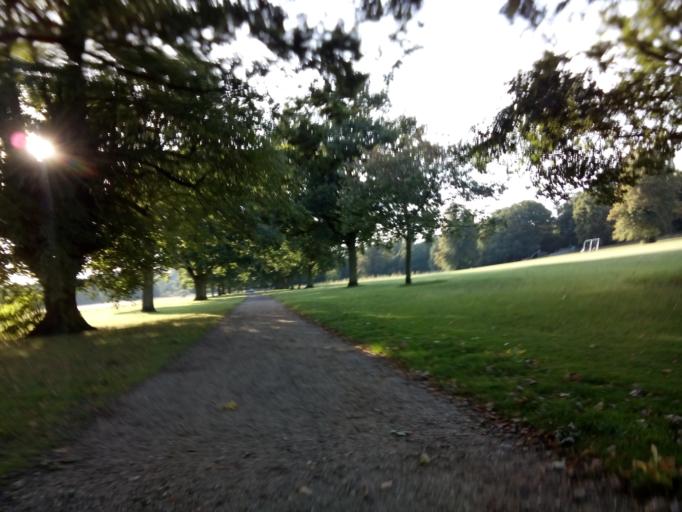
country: GB
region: England
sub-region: Suffolk
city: Ipswich
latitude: 52.0342
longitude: 1.1402
